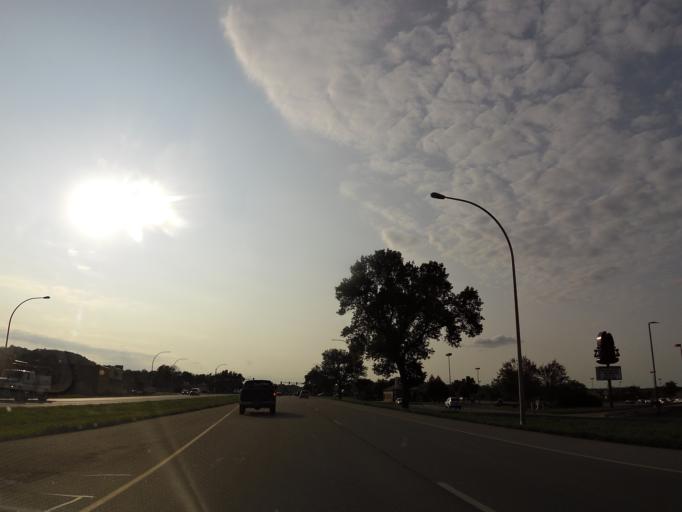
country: US
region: Minnesota
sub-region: Goodhue County
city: Red Wing
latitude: 44.5672
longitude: -92.5819
